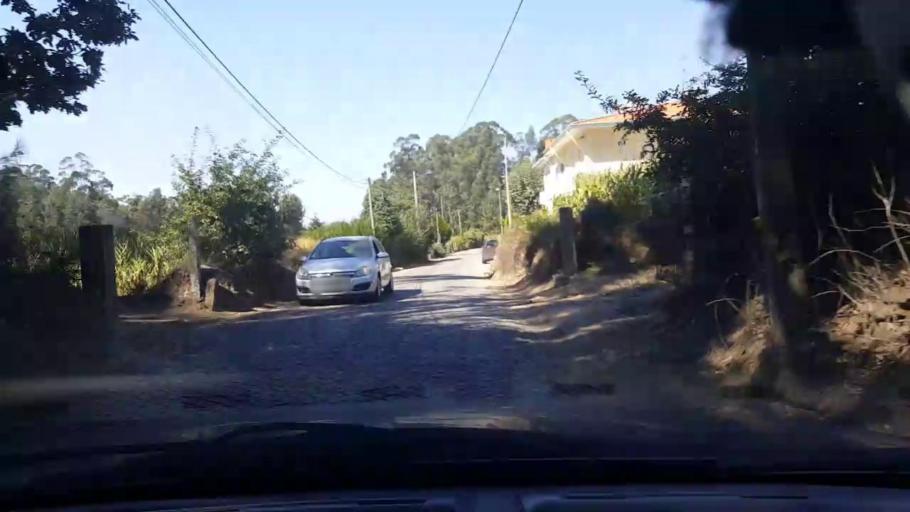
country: PT
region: Porto
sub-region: Matosinhos
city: Lavra
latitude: 41.2739
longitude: -8.6960
